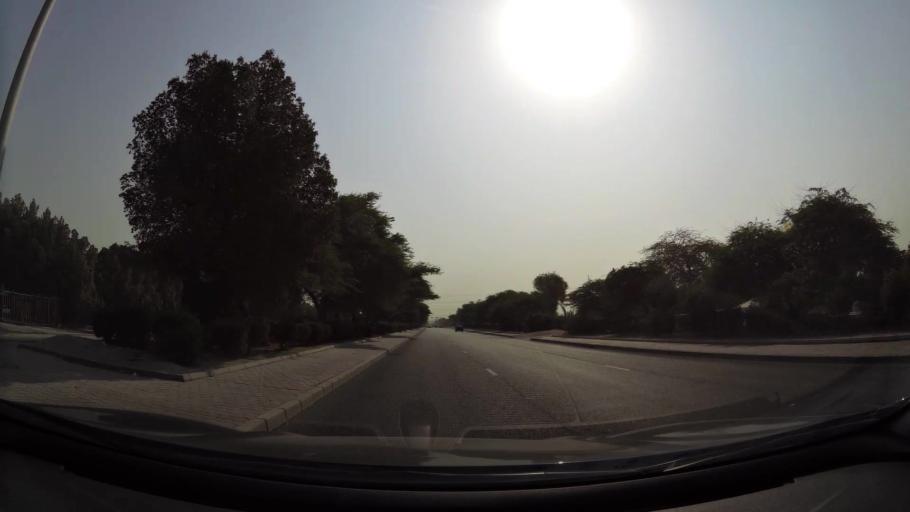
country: KW
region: Al Asimah
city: Ar Rabiyah
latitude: 29.2794
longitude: 47.8393
